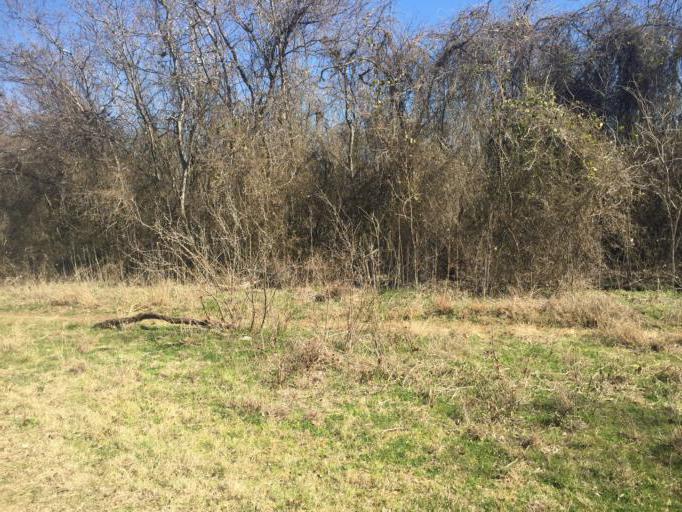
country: US
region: Texas
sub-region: Travis County
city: Onion Creek
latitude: 30.1571
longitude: -97.8059
